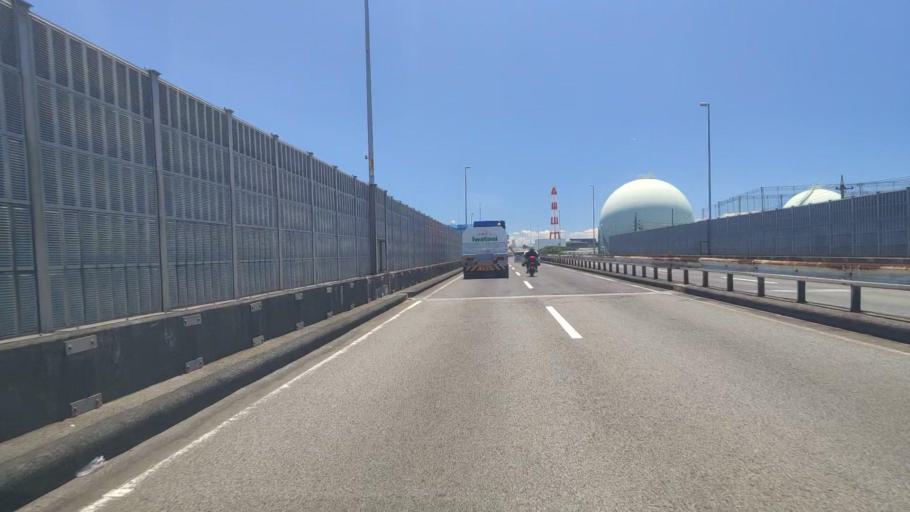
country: JP
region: Mie
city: Yokkaichi
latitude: 34.9514
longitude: 136.6239
